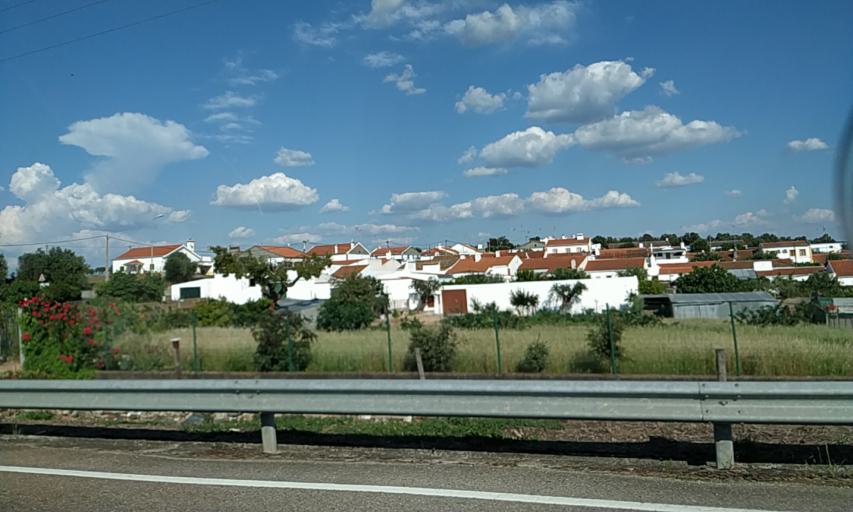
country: PT
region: Evora
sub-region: Estremoz
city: Estremoz
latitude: 38.9600
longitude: -7.5098
